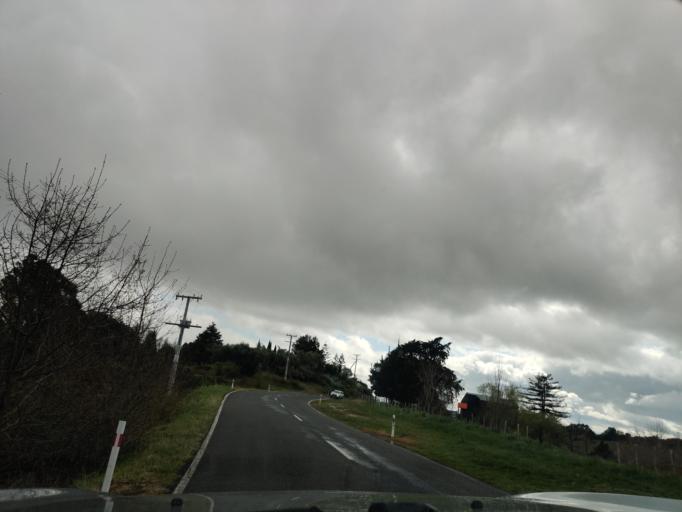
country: NZ
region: Hawke's Bay
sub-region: Hastings District
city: Hastings
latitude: -39.6849
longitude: 176.8985
